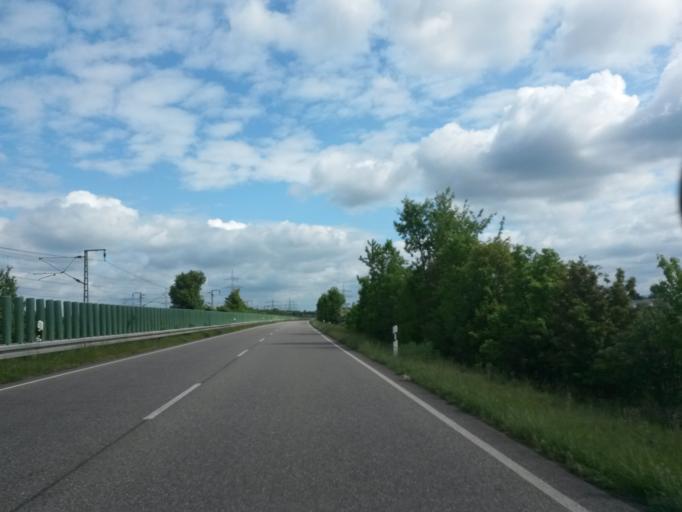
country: DE
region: Baden-Wuerttemberg
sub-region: Karlsruhe Region
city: Waghausel
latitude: 49.2429
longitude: 8.4975
